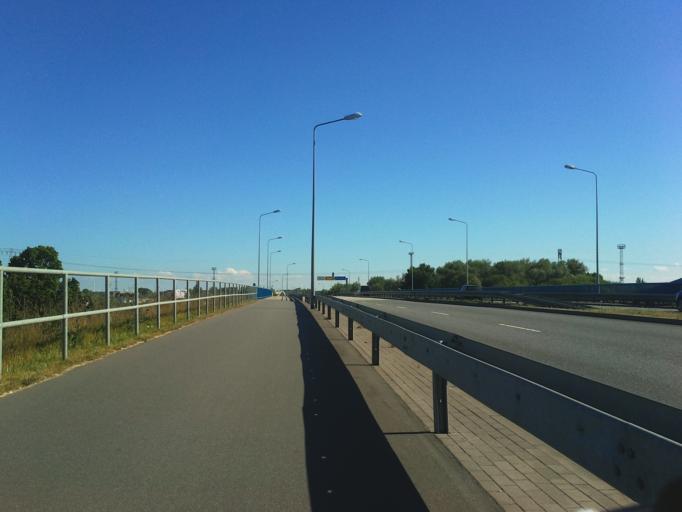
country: DE
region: Mecklenburg-Vorpommern
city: Dierkow-Neu
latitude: 54.1196
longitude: 12.1663
